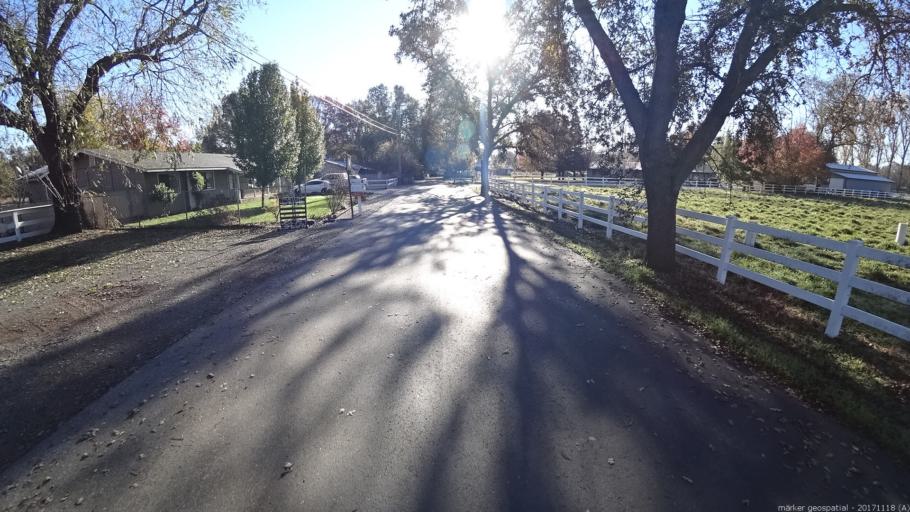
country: US
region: California
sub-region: Shasta County
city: Anderson
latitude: 40.4538
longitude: -122.2390
